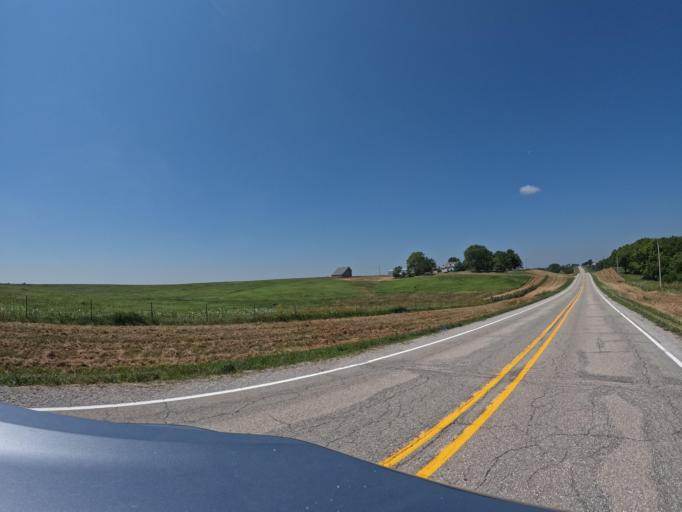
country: US
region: Iowa
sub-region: Keokuk County
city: Sigourney
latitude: 41.2649
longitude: -92.2135
